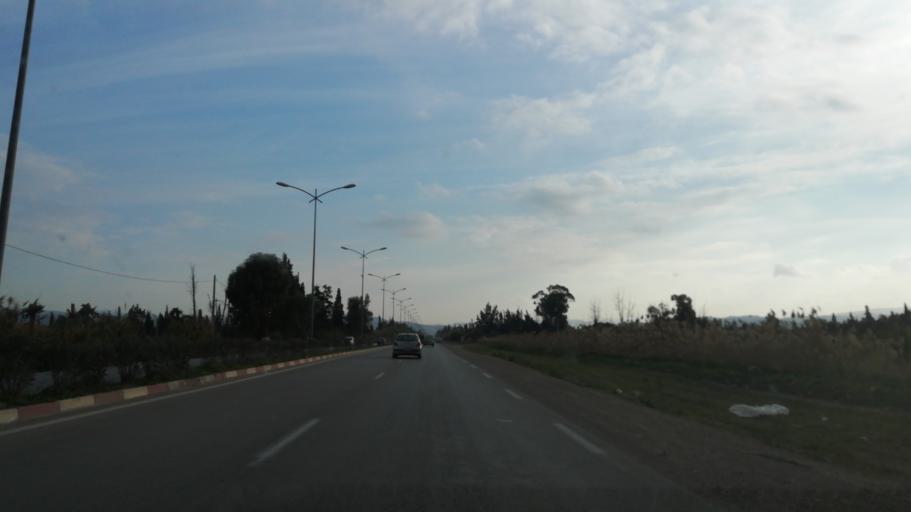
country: DZ
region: Mascara
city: Mascara
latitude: 35.6209
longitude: 0.0620
